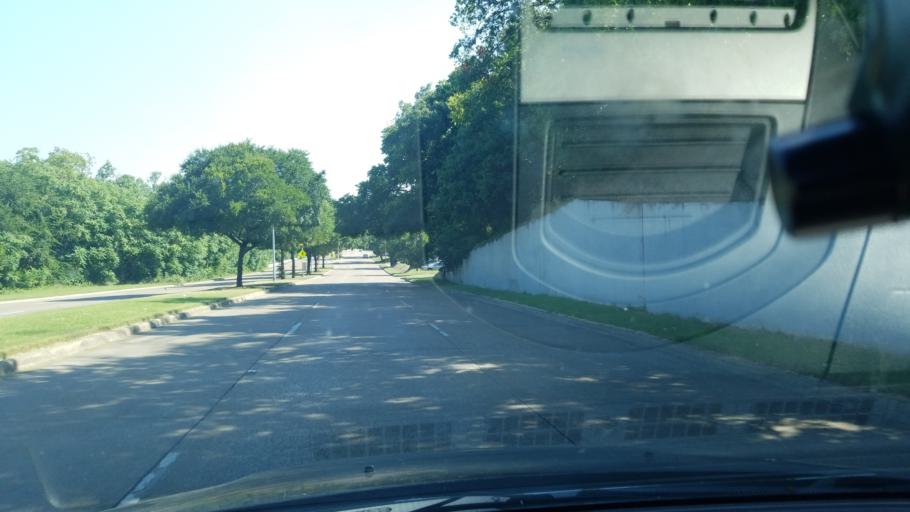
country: US
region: Texas
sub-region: Dallas County
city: Dallas
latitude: 32.7336
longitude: -96.7999
